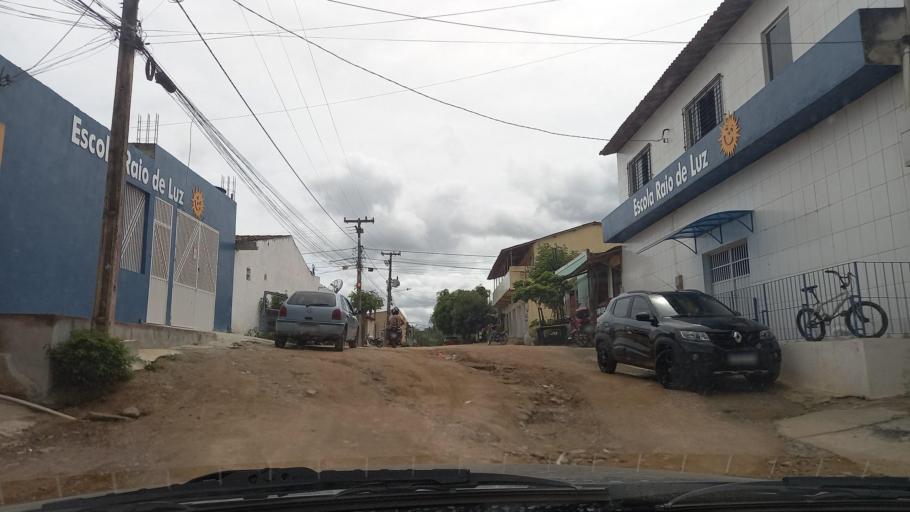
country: ET
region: Oromiya
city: Gore
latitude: 8.1944
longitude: 35.5800
